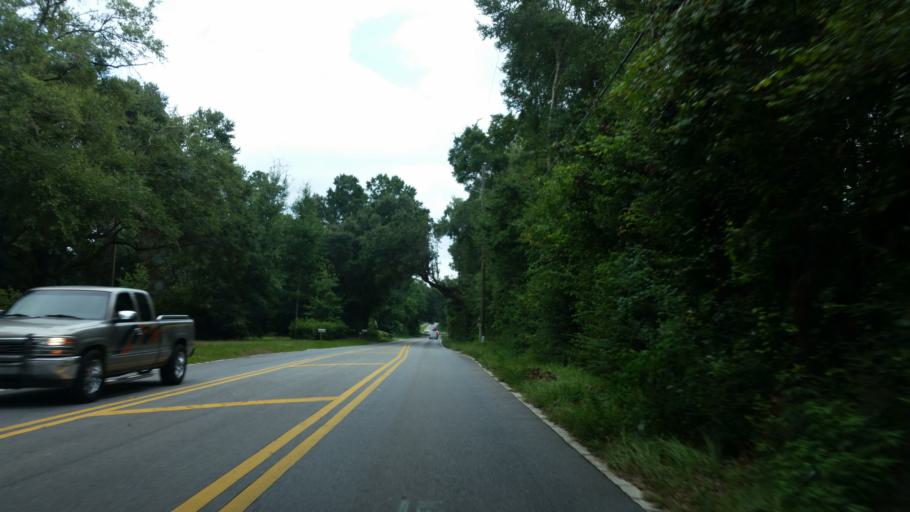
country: US
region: Florida
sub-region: Santa Rosa County
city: Pace
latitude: 30.6361
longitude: -87.1480
